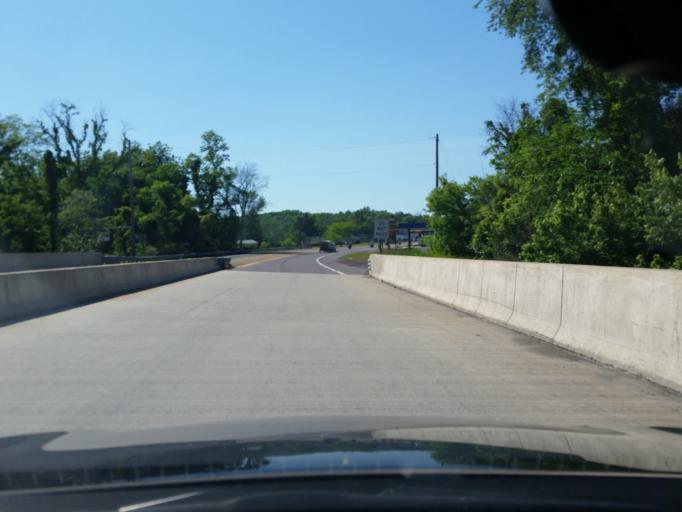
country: US
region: Pennsylvania
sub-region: Northumberland County
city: Dewart
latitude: 41.1004
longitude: -76.8911
